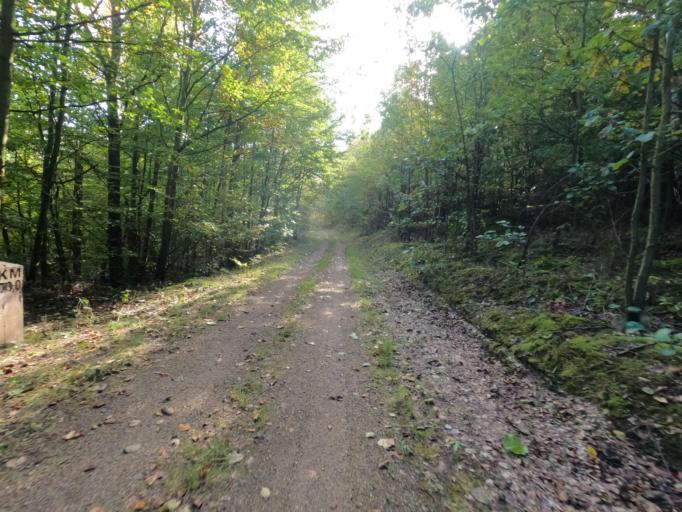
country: DE
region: North Rhine-Westphalia
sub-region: Regierungsbezirk Koln
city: Inden
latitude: 50.8590
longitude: 6.3180
